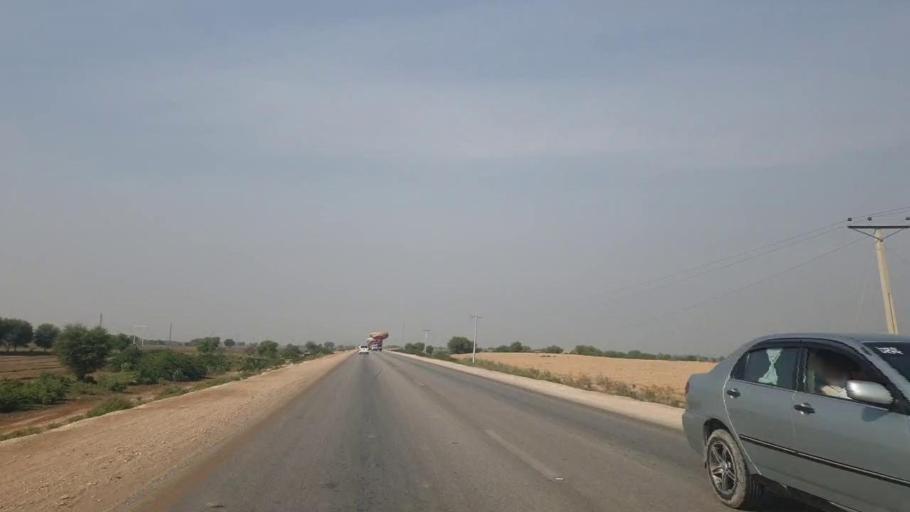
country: PK
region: Sindh
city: Sann
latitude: 26.0679
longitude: 68.1004
